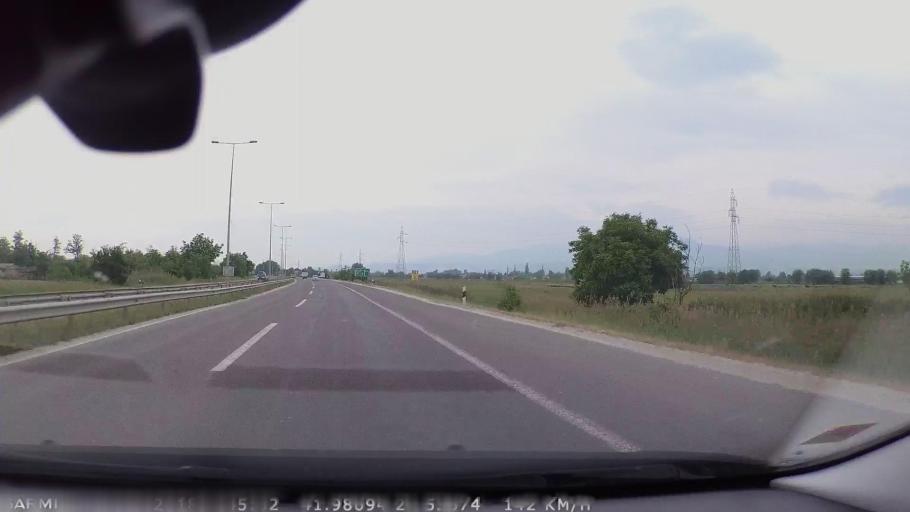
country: MK
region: Ilinden
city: Jurumleri
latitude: 41.9857
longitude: 21.5374
